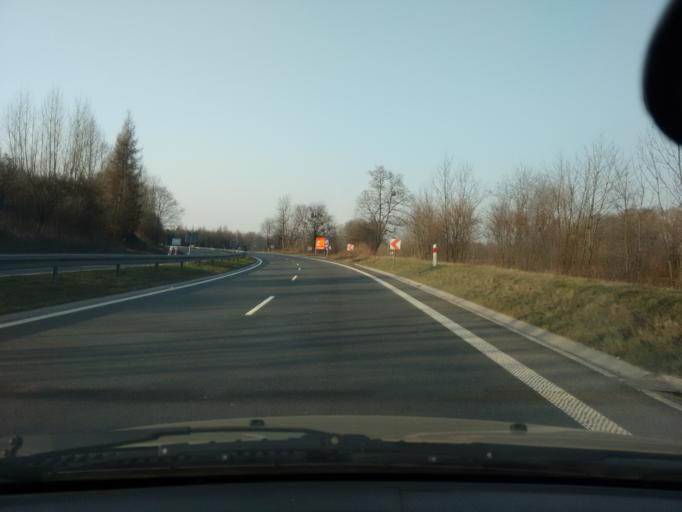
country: PL
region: Silesian Voivodeship
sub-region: Powiat cieszynski
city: Ochaby
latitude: 49.8295
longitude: 18.7876
